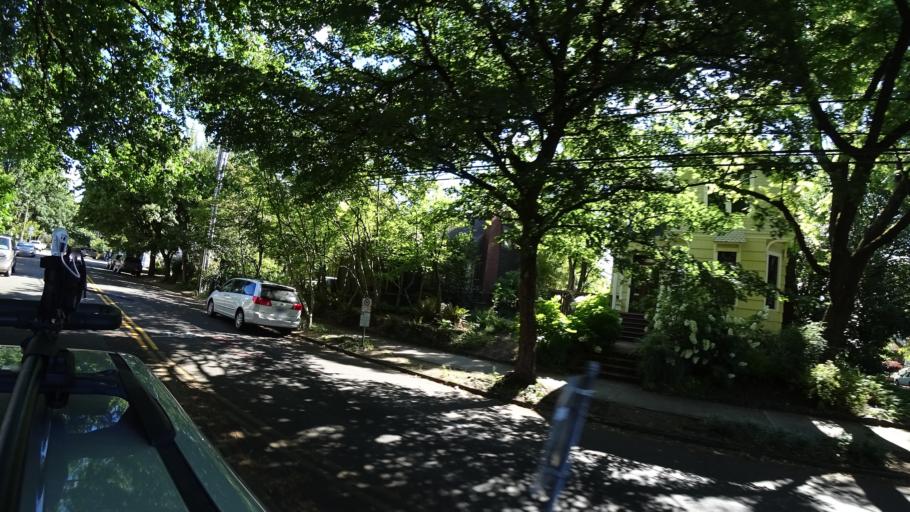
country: US
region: Oregon
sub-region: Multnomah County
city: Portland
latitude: 45.4982
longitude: -122.6759
